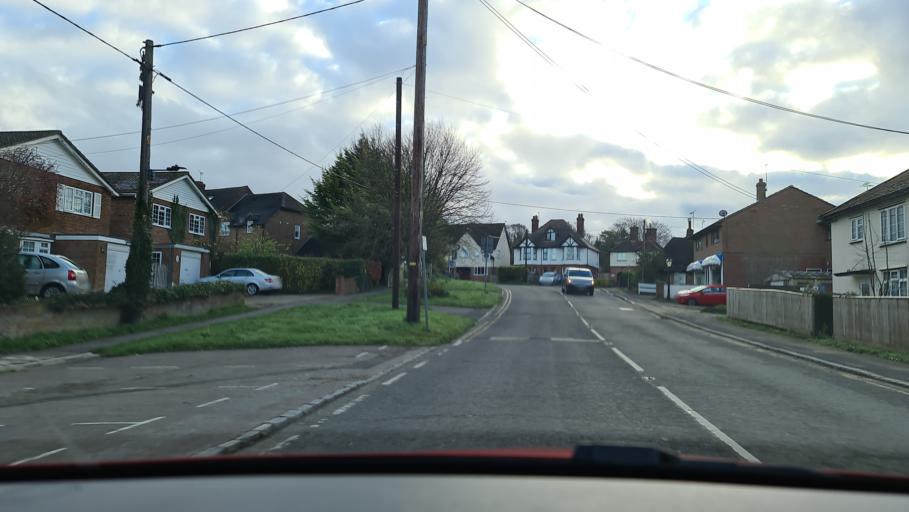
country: GB
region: England
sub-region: Buckinghamshire
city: Princes Risborough
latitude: 51.7184
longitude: -0.8414
